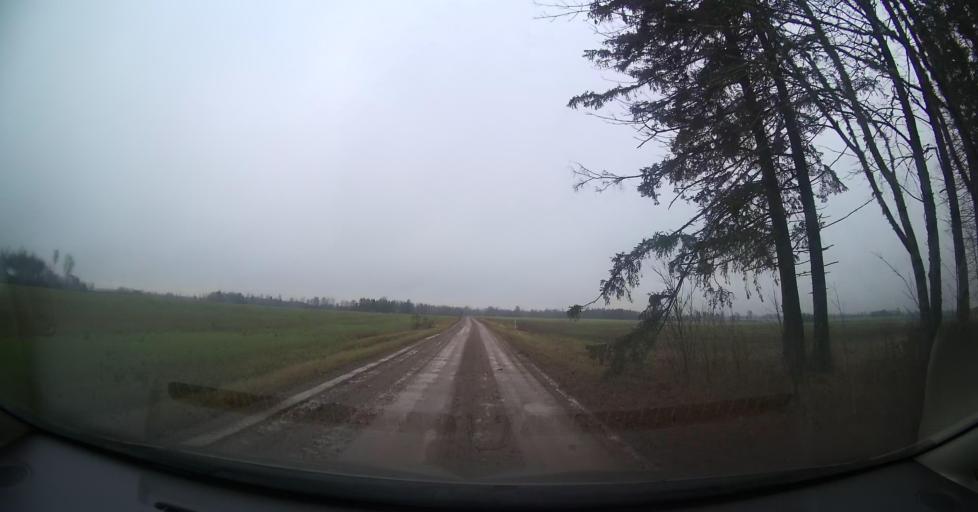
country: EE
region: Tartu
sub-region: Tartu linn
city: Tartu
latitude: 58.3844
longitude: 26.9271
